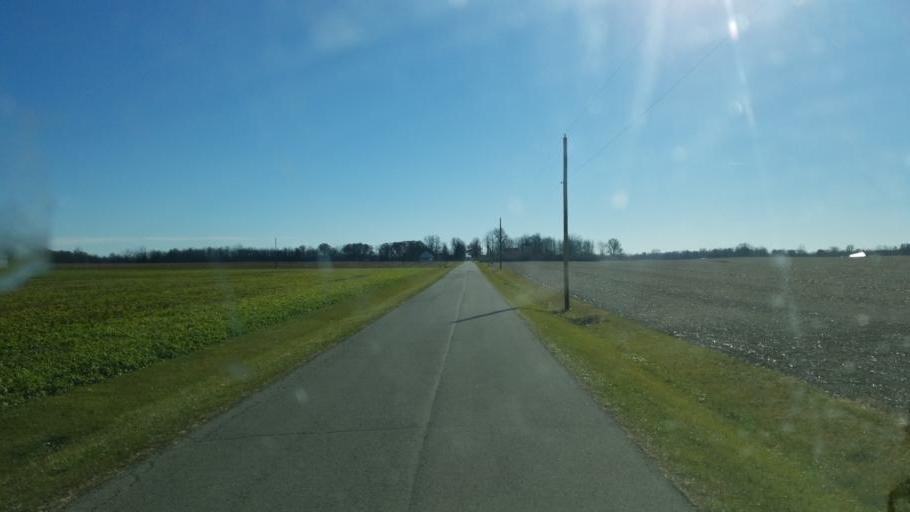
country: US
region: Ohio
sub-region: Crawford County
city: Galion
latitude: 40.7551
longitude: -82.8389
